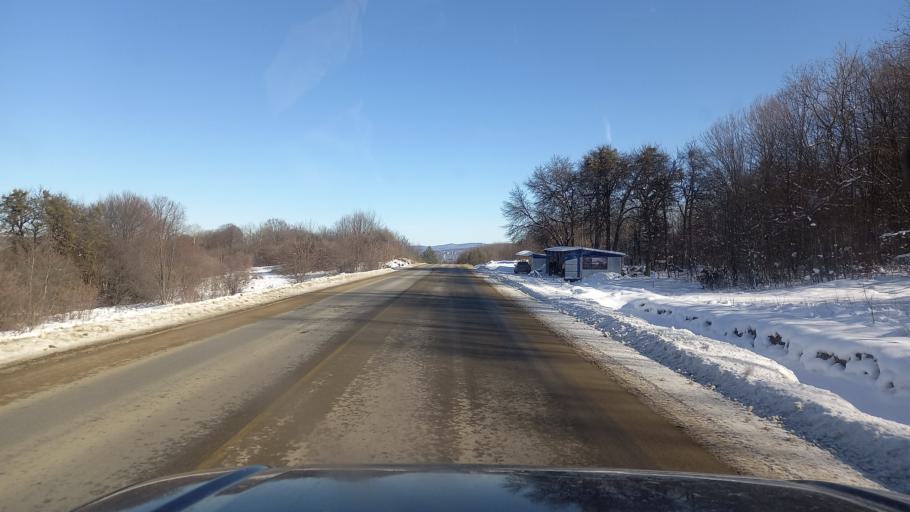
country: RU
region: Adygeya
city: Kamennomostskiy
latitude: 44.2205
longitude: 40.0913
